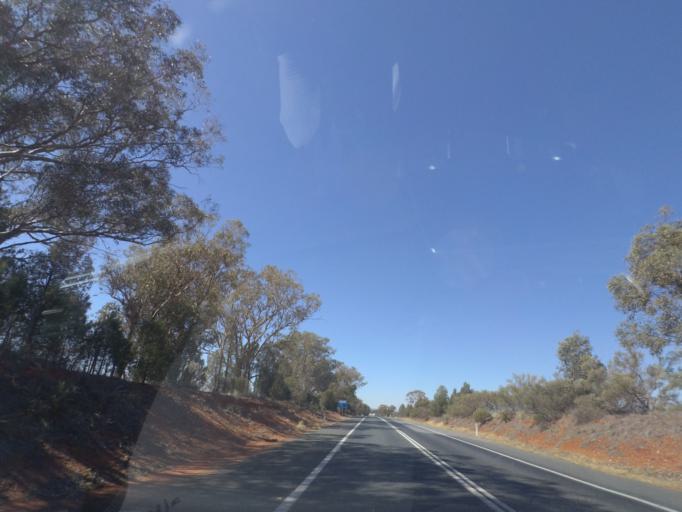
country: AU
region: New South Wales
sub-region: Bland
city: West Wyalong
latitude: -34.1799
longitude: 147.1136
